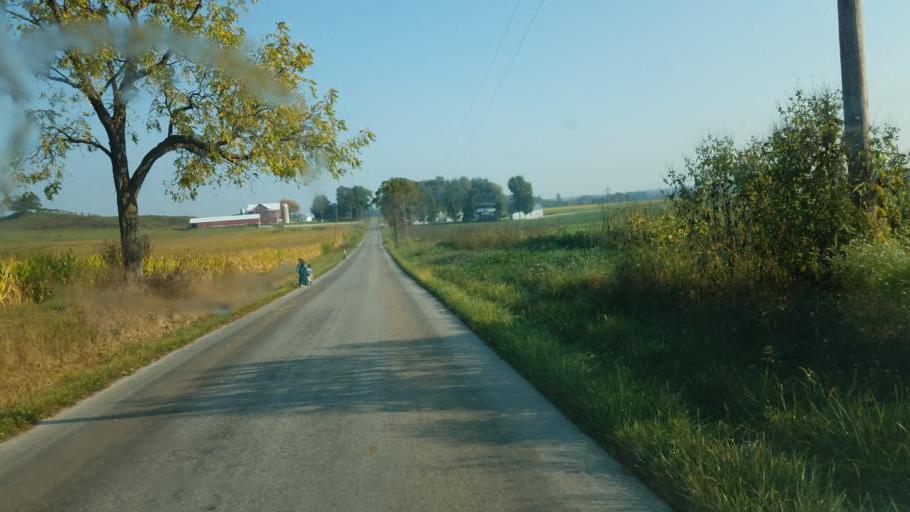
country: US
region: Ohio
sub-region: Knox County
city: Fredericktown
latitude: 40.5160
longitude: -82.6045
